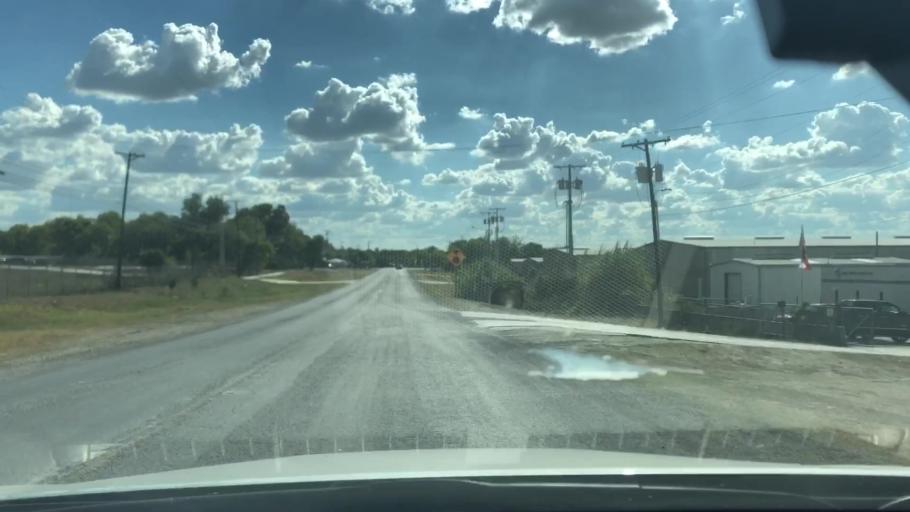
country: US
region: Texas
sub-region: Comal County
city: New Braunfels
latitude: 29.6676
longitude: -98.1683
